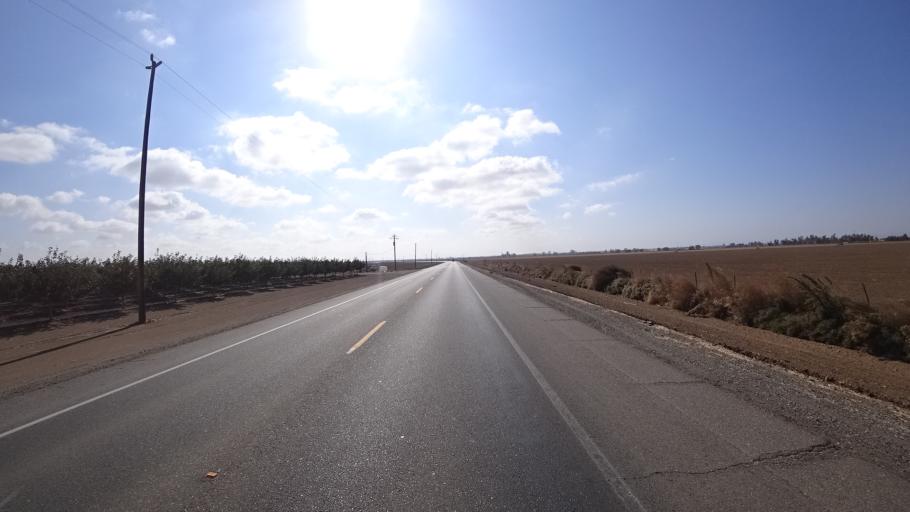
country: US
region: California
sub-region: Yolo County
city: Woodland
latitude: 38.7205
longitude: -121.7303
